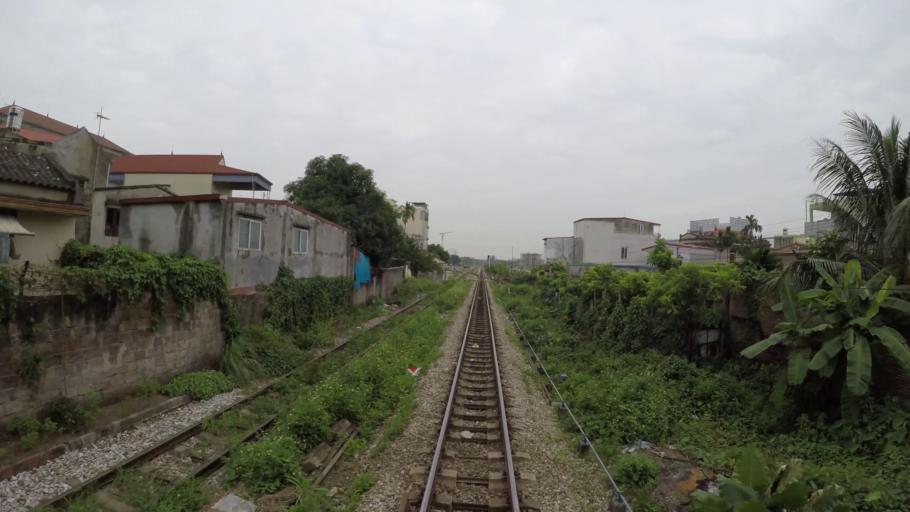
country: VN
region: Hai Phong
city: An Duong
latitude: 20.8844
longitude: 106.6042
